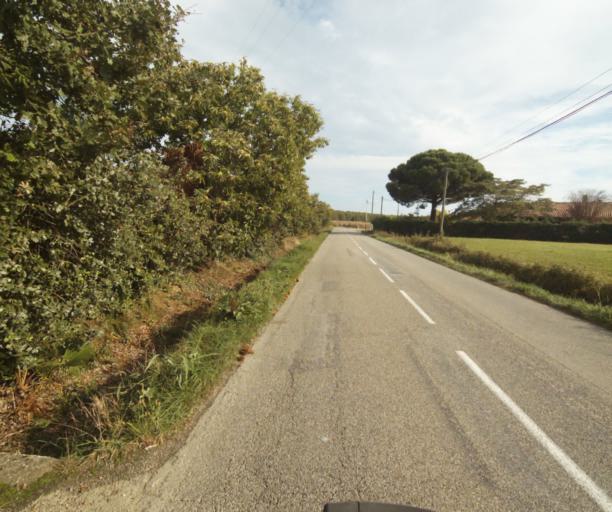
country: FR
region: Midi-Pyrenees
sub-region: Departement du Tarn-et-Garonne
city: Montech
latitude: 43.9767
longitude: 1.2331
